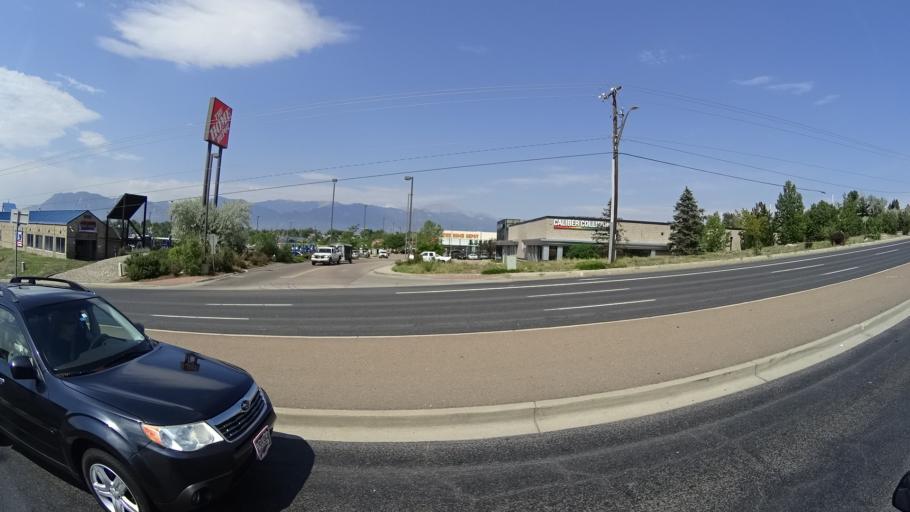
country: US
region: Colorado
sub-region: El Paso County
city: Cimarron Hills
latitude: 38.8339
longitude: -104.7575
